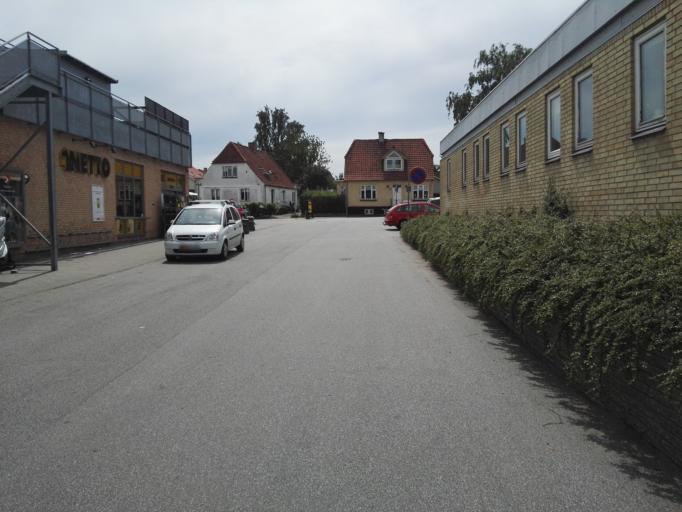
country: DK
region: Capital Region
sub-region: Hillerod Kommune
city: Skaevinge
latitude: 55.9091
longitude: 12.1494
